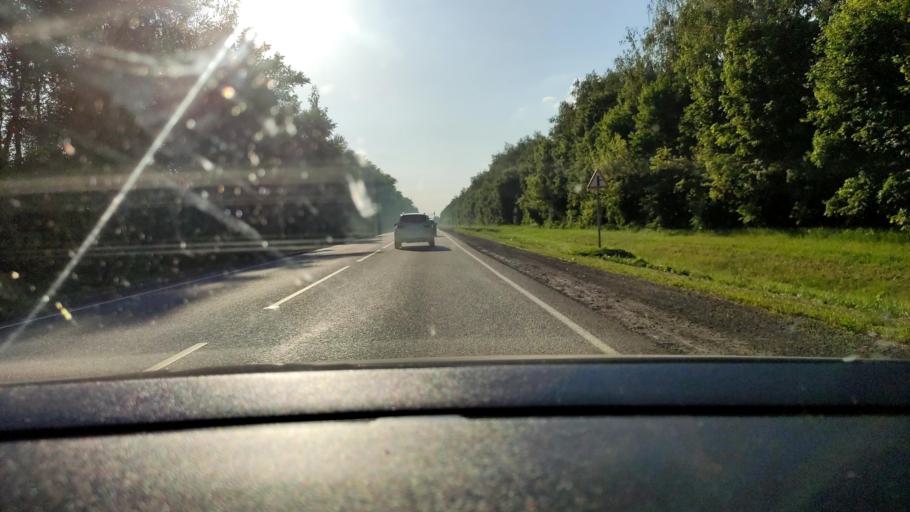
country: RU
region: Voronezj
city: Kashirskoye
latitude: 51.4689
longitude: 39.7008
